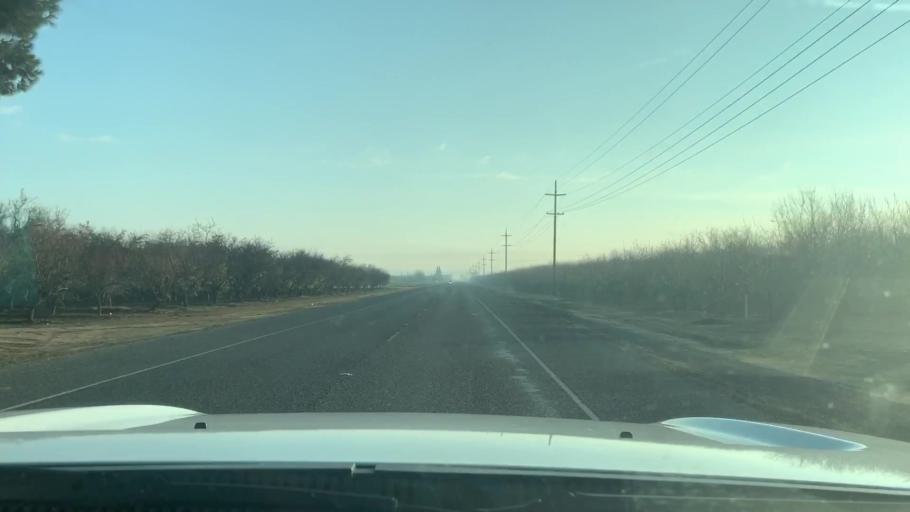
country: US
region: California
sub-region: Kern County
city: Wasco
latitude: 35.6015
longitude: -119.3827
